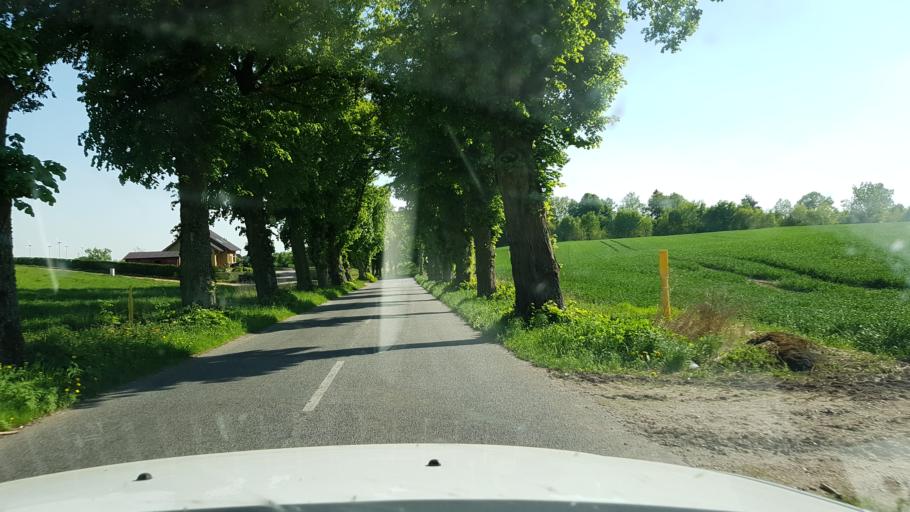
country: PL
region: West Pomeranian Voivodeship
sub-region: Powiat lobeski
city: Resko
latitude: 53.7813
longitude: 15.4097
